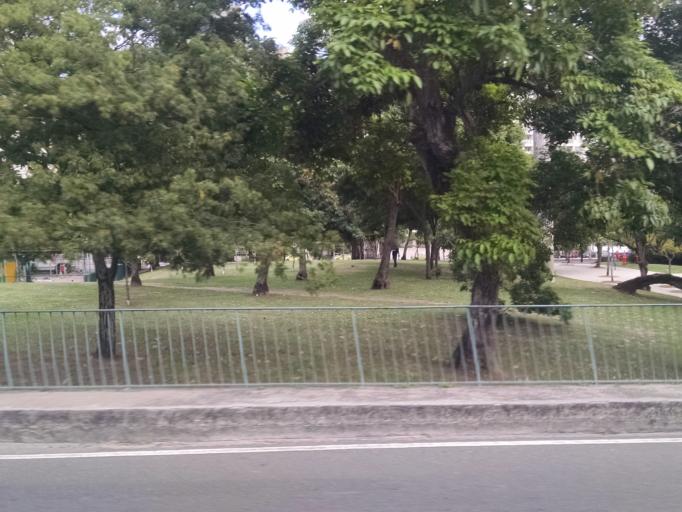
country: BR
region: Rio de Janeiro
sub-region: Rio De Janeiro
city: Rio de Janeiro
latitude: -22.9302
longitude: -43.1730
